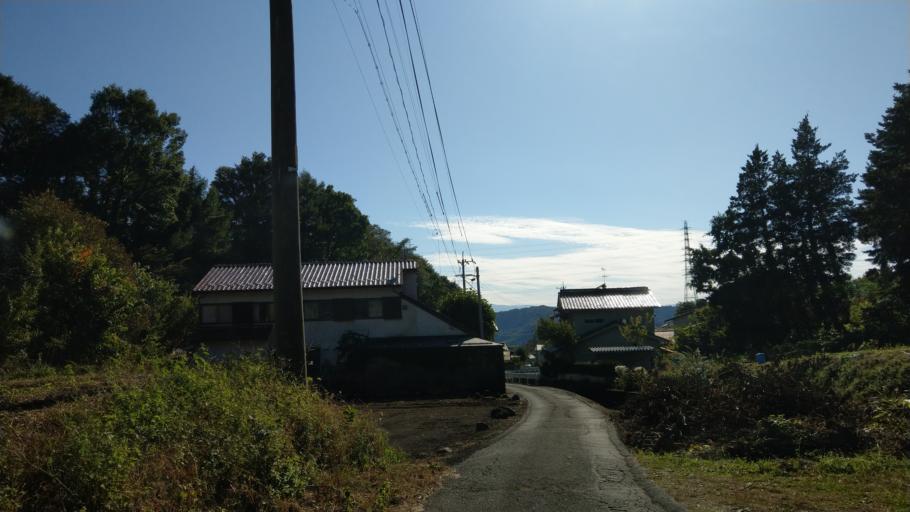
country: JP
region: Nagano
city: Komoro
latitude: 36.3355
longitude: 138.4327
